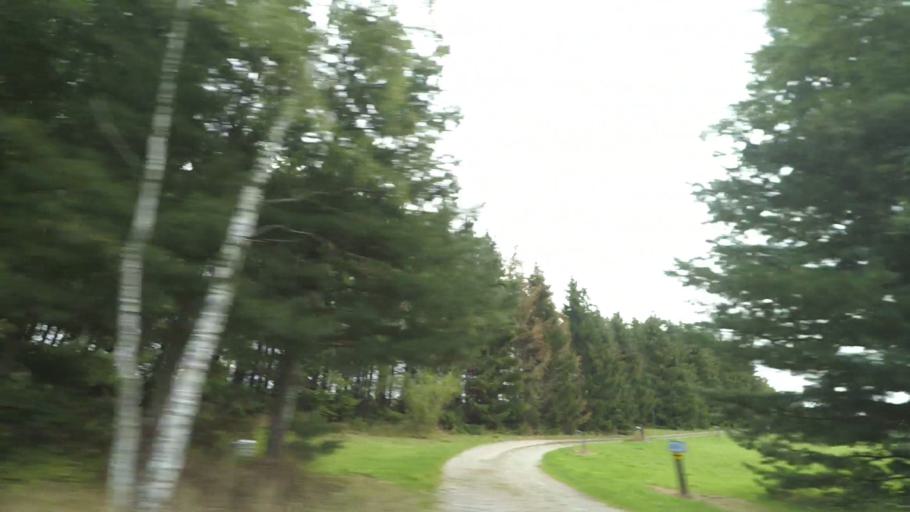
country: DK
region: Central Jutland
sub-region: Syddjurs Kommune
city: Ryomgard
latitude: 56.4342
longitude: 10.5652
